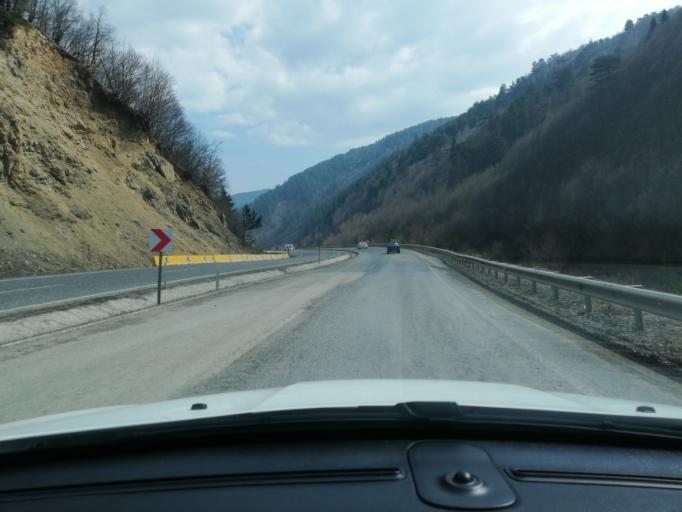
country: TR
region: Kastamonu
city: Kuzyaka
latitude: 41.1196
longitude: 33.7572
